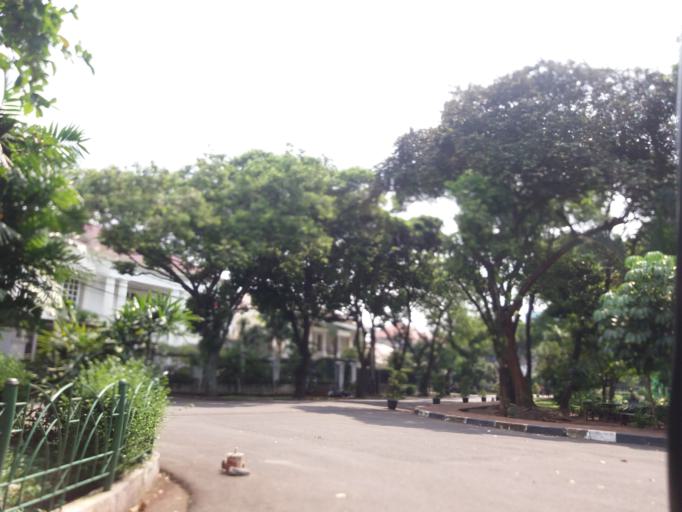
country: ID
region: Jakarta Raya
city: Jakarta
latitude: -6.2343
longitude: 106.8024
